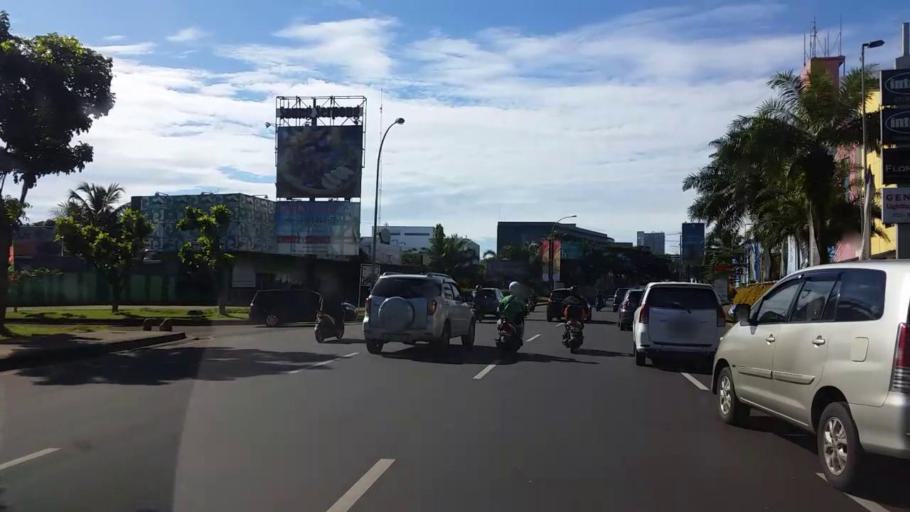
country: ID
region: West Java
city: Serpong
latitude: -6.2849
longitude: 106.6658
